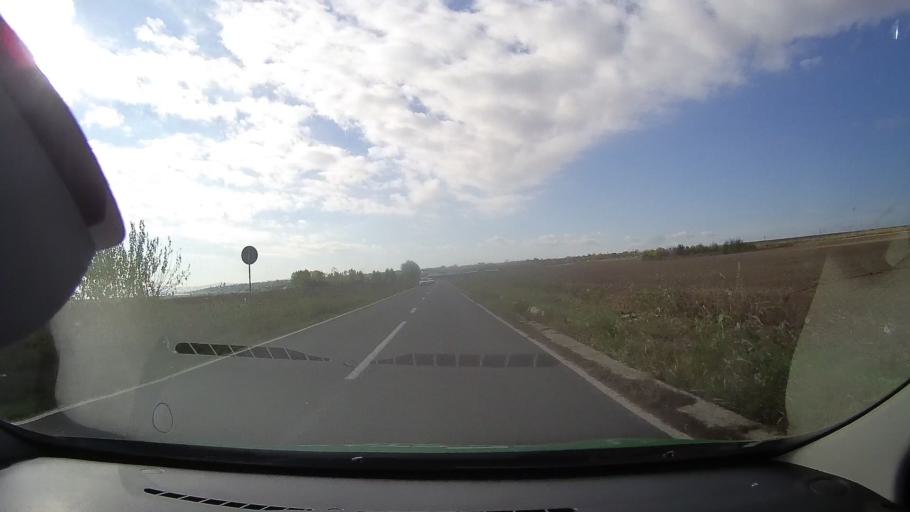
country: RO
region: Tulcea
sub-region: Comuna Sarichioi
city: Sarichioi
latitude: 44.9615
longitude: 28.8603
